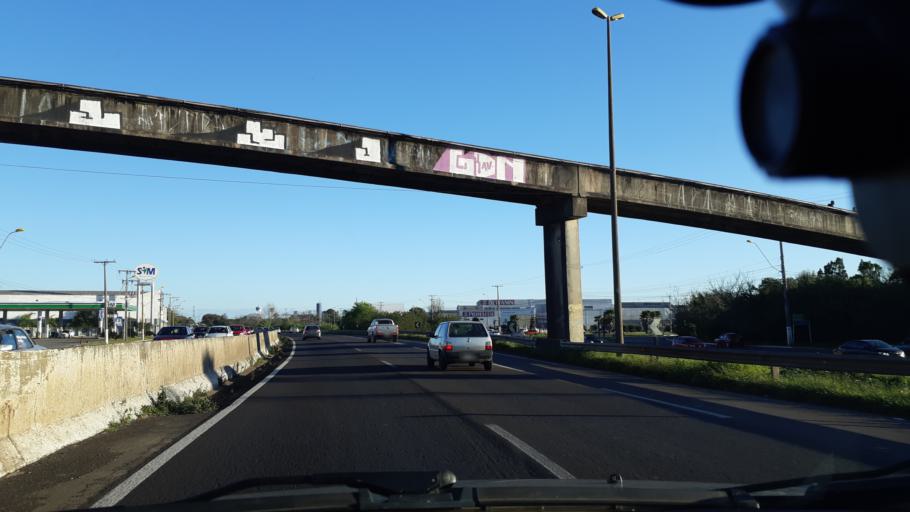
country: BR
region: Rio Grande do Sul
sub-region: Esteio
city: Esteio
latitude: -29.8595
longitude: -51.1810
